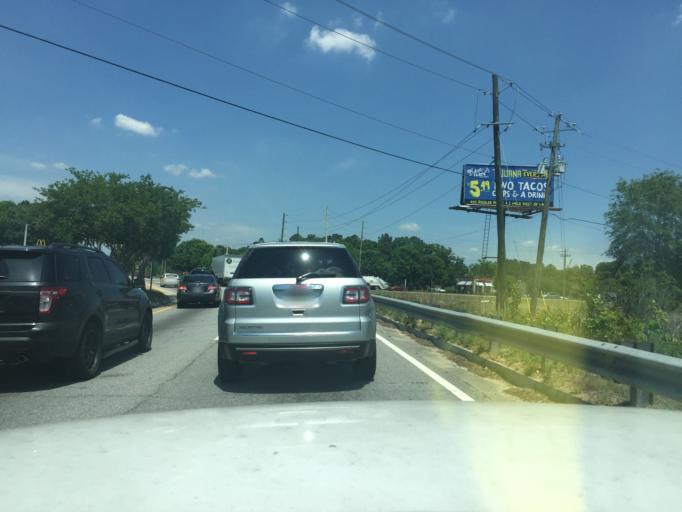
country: US
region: Georgia
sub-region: Chatham County
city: Garden City
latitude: 32.0473
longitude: -81.1652
